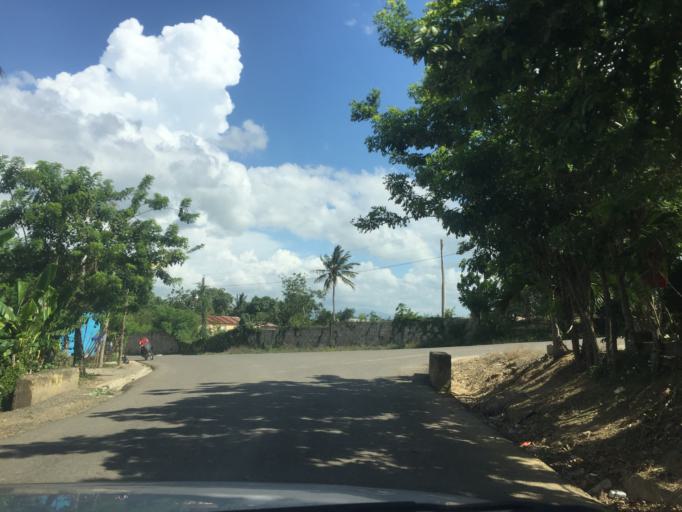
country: DO
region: La Vega
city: Rio Verde Arriba
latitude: 19.3555
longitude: -70.5905
